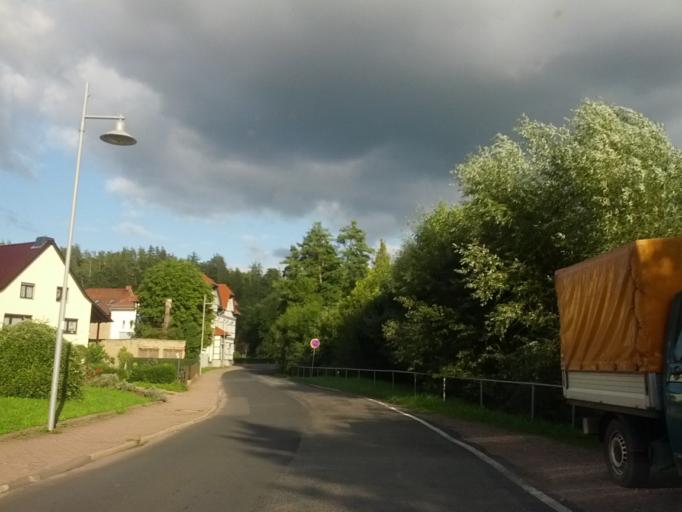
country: DE
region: Thuringia
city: Wolfsburg-Unkeroda
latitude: 50.9374
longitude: 10.2659
